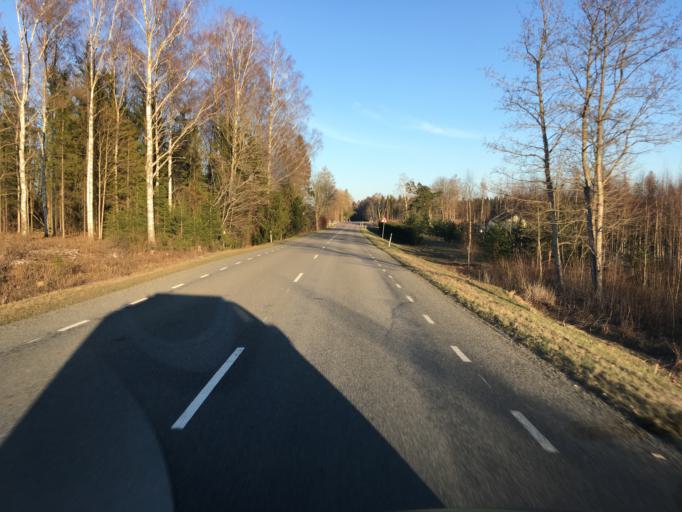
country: EE
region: Raplamaa
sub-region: Rapla vald
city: Rapla
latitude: 59.0694
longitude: 24.9105
